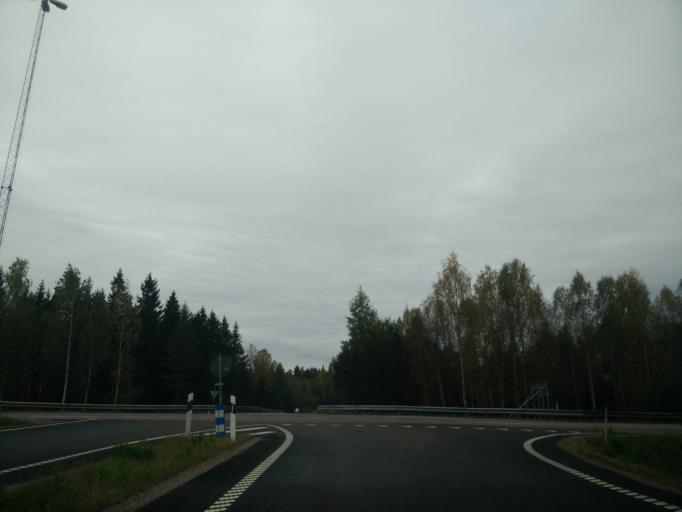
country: SE
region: Gaevleborg
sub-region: Gavle Kommun
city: Norrsundet
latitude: 60.9021
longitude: 17.0148
